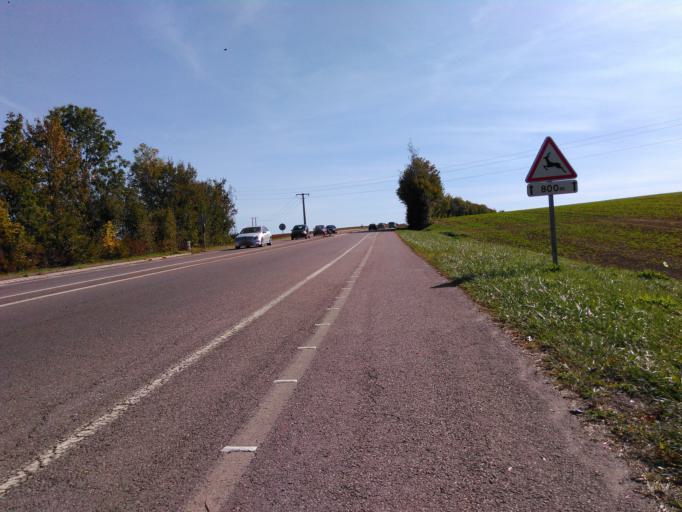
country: FR
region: Lorraine
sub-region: Departement de la Moselle
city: Hettange-Grande
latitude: 49.3928
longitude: 6.1669
